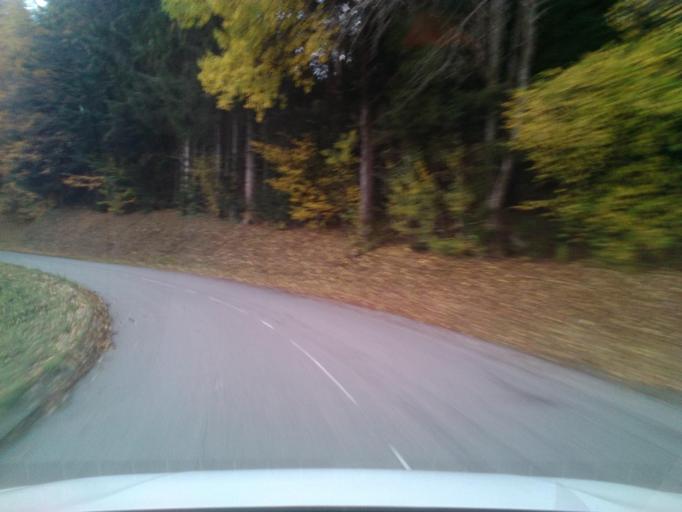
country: FR
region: Lorraine
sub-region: Departement des Vosges
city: Plainfaing
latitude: 48.2037
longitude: 7.0343
